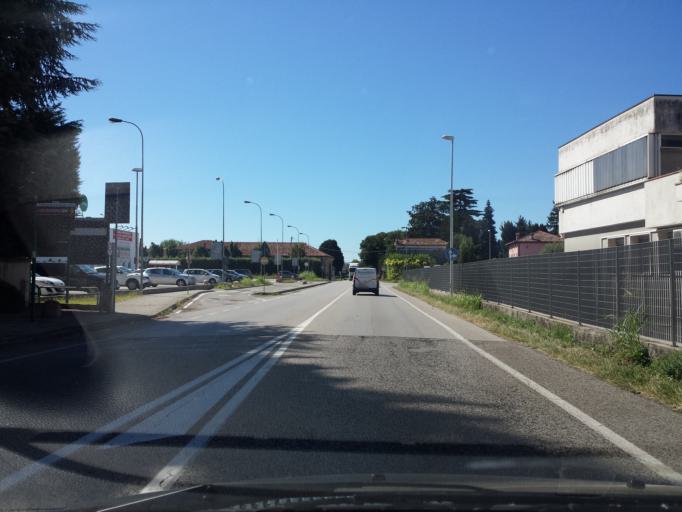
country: IT
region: Veneto
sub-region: Provincia di Vicenza
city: Dueville
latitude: 45.6233
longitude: 11.5692
